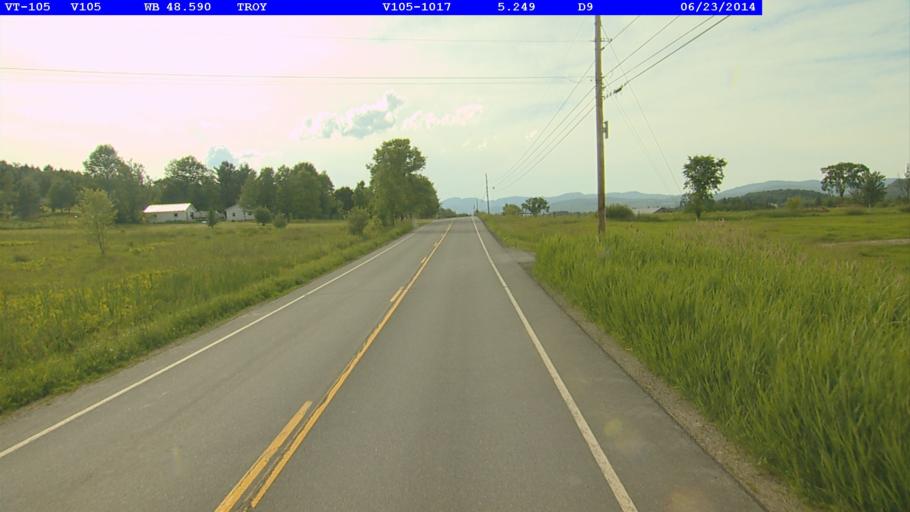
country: US
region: Vermont
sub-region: Orleans County
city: Newport
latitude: 44.9826
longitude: -72.3563
